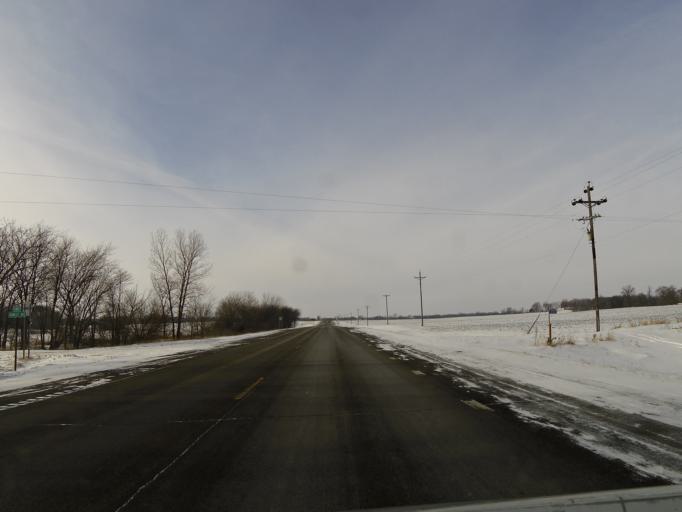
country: US
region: Minnesota
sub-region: McLeod County
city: Lester Prairie
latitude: 44.9068
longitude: -94.1748
